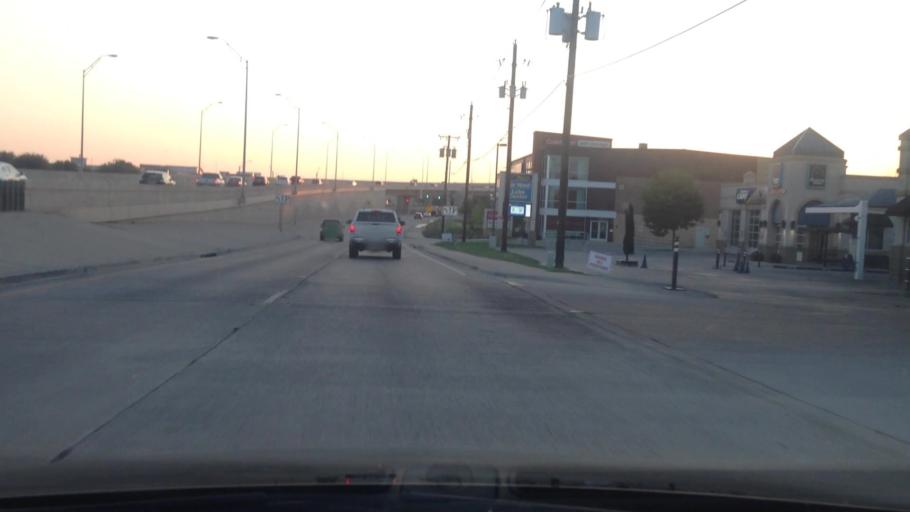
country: US
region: Texas
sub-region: Tarrant County
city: Grapevine
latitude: 32.9291
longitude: -97.1009
